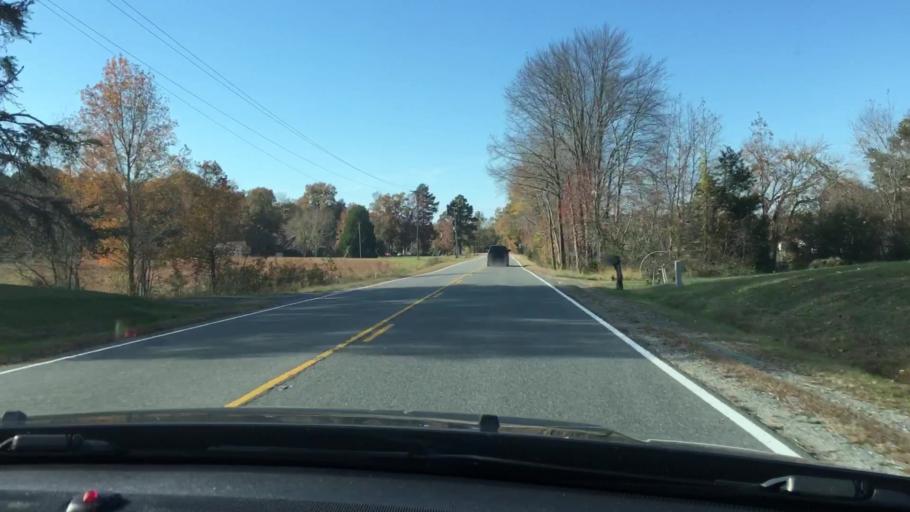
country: US
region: Virginia
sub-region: Hanover County
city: Hanover
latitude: 37.8298
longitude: -77.3520
